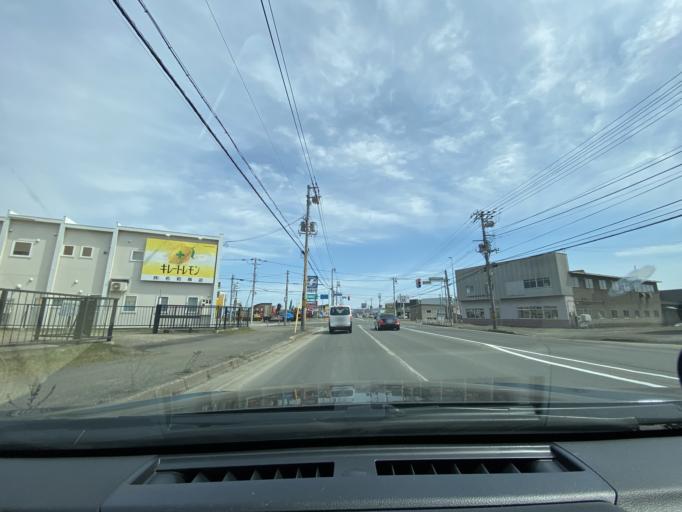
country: JP
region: Hokkaido
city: Kitami
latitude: 43.7996
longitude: 143.8283
